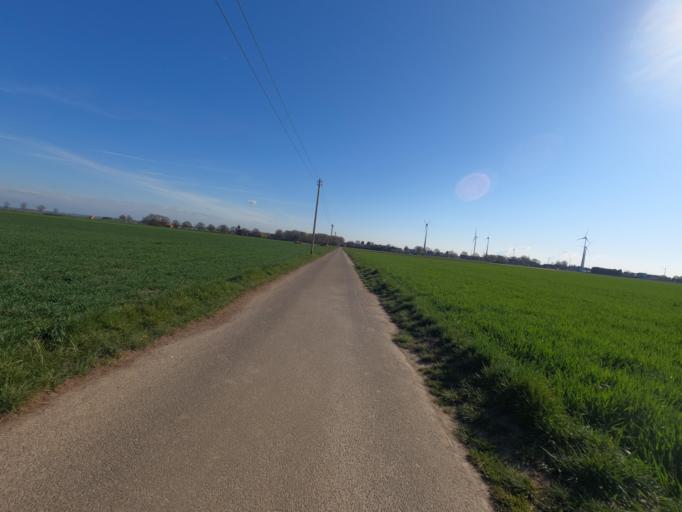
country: DE
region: North Rhine-Westphalia
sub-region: Regierungsbezirk Koln
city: Heinsberg
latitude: 51.0178
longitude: 6.0809
